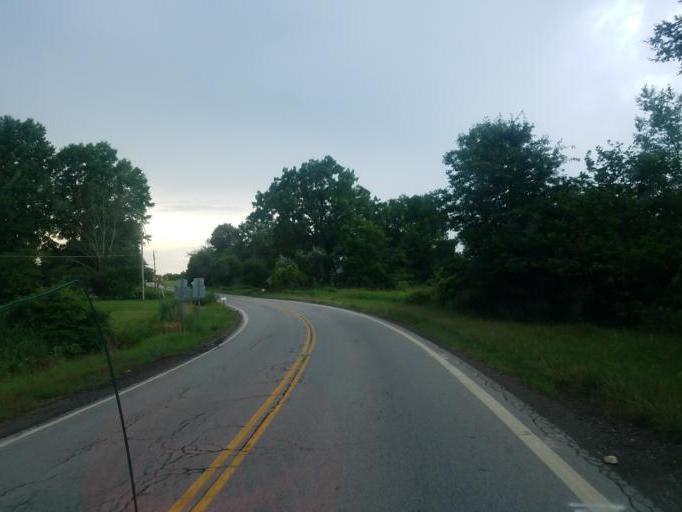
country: US
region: Ohio
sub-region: Wayne County
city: Rittman
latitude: 40.9458
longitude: -81.7456
